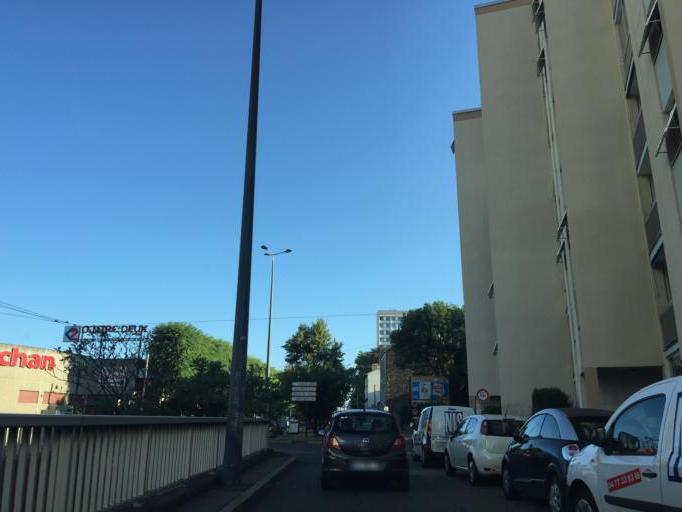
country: FR
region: Rhone-Alpes
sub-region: Departement de la Loire
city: Saint-Etienne
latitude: 45.4220
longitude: 4.3967
